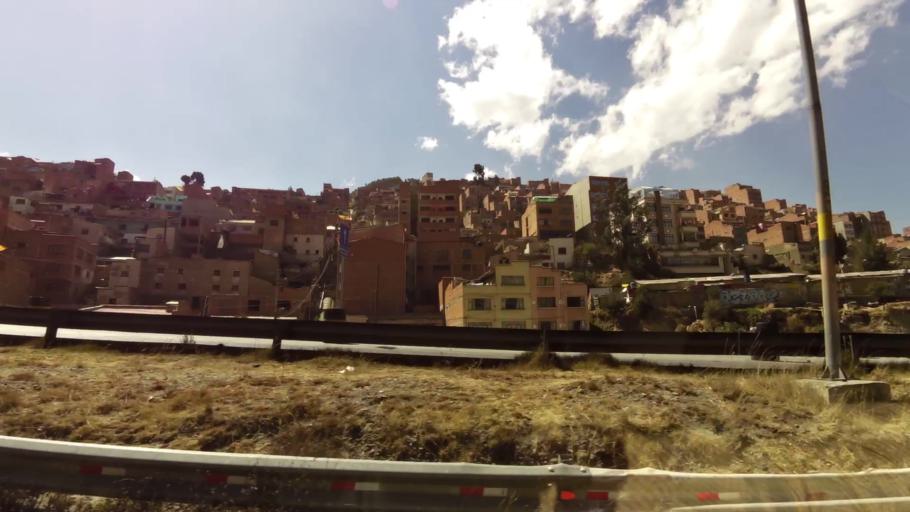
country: BO
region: La Paz
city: La Paz
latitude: -16.4810
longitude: -68.1483
